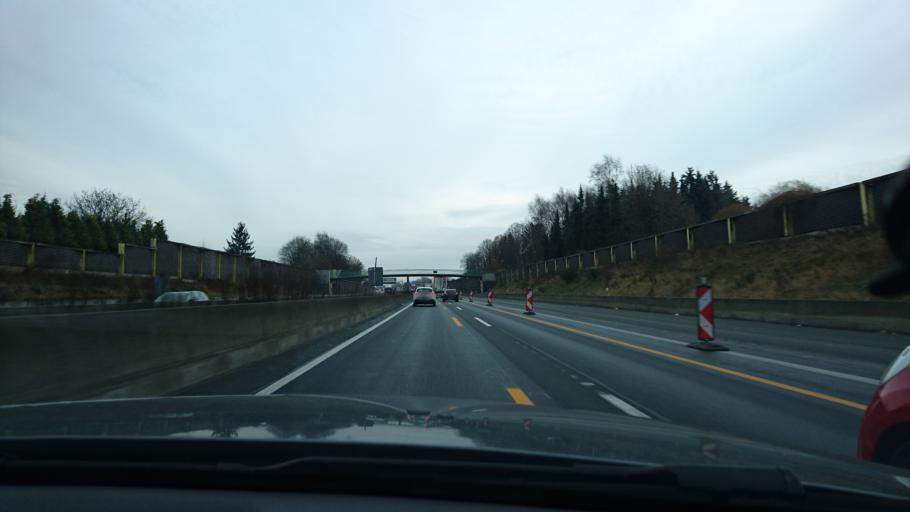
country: DE
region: North Rhine-Westphalia
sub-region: Regierungsbezirk Munster
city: Lotte
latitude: 52.2854
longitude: 7.9386
